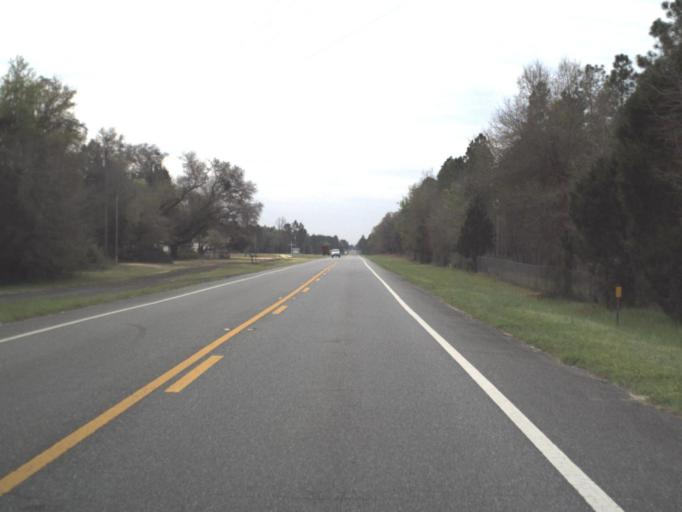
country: US
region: Florida
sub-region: Calhoun County
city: Blountstown
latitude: 30.5096
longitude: -85.2003
